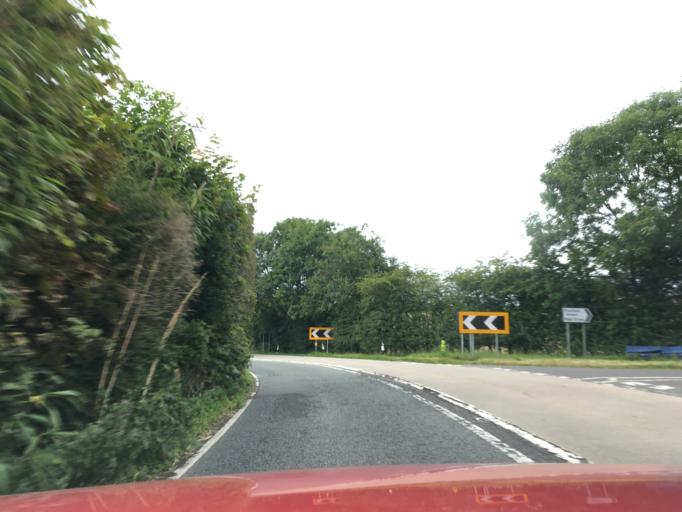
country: GB
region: England
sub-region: Hampshire
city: Petersfield
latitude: 51.0153
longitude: -1.0043
